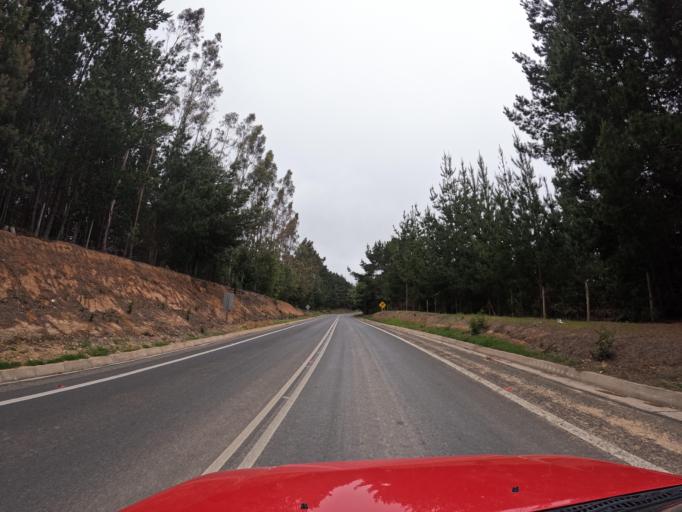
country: CL
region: O'Higgins
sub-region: Provincia de Colchagua
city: Santa Cruz
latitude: -34.6049
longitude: -72.0154
